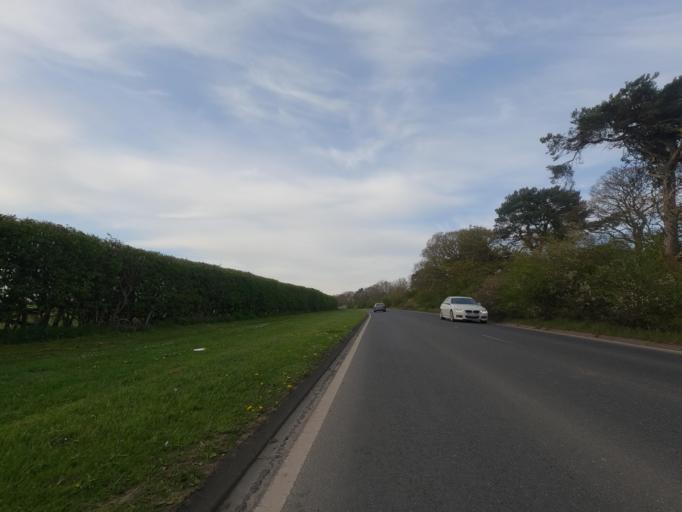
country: GB
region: England
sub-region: Newcastle upon Tyne
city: Dinnington
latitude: 55.0341
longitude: -1.6653
